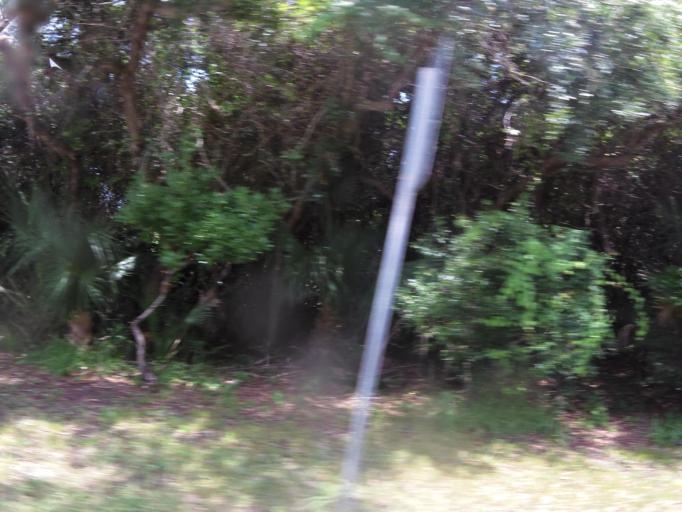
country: US
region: Florida
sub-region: Volusia County
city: Ponce Inlet
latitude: 29.0825
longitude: -80.9251
